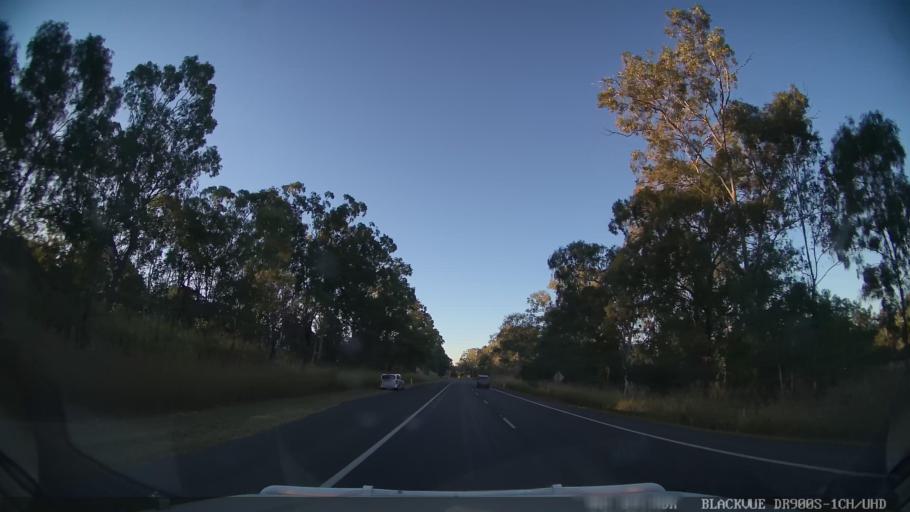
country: AU
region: Queensland
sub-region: Gladstone
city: Toolooa
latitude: -23.9588
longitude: 151.2191
